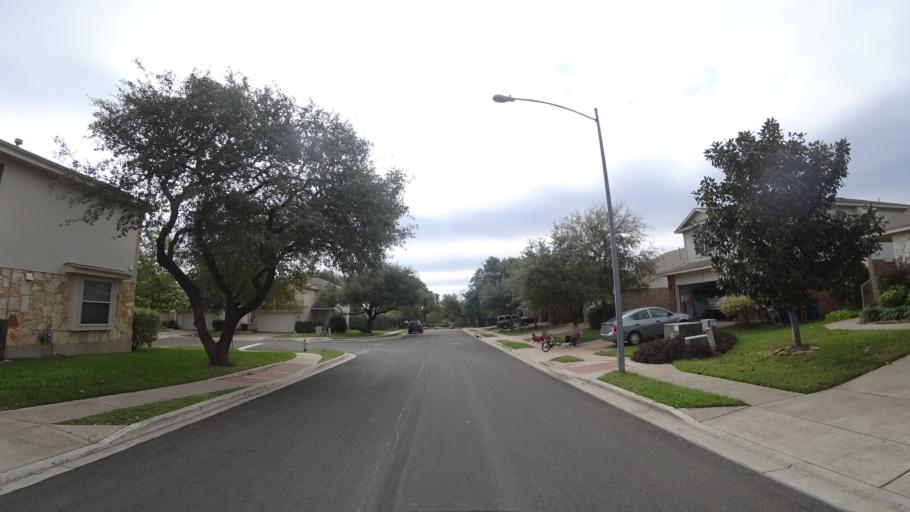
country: US
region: Texas
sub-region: Travis County
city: Manchaca
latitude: 30.1522
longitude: -97.8455
